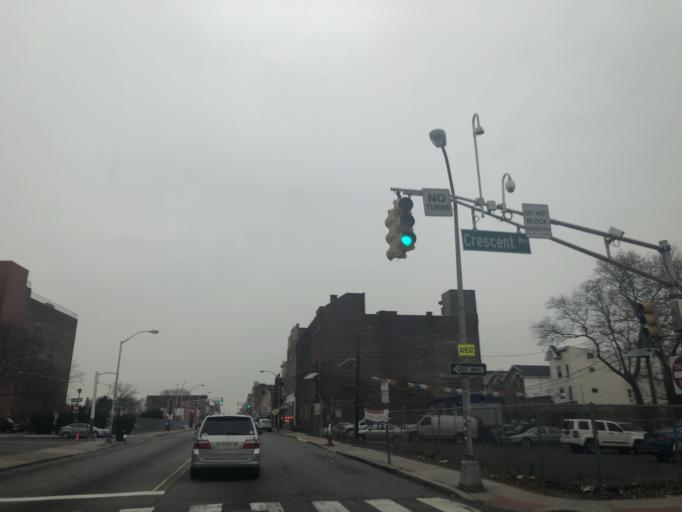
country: US
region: New Jersey
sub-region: Hudson County
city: Jersey City
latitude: 40.7166
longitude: -74.0709
